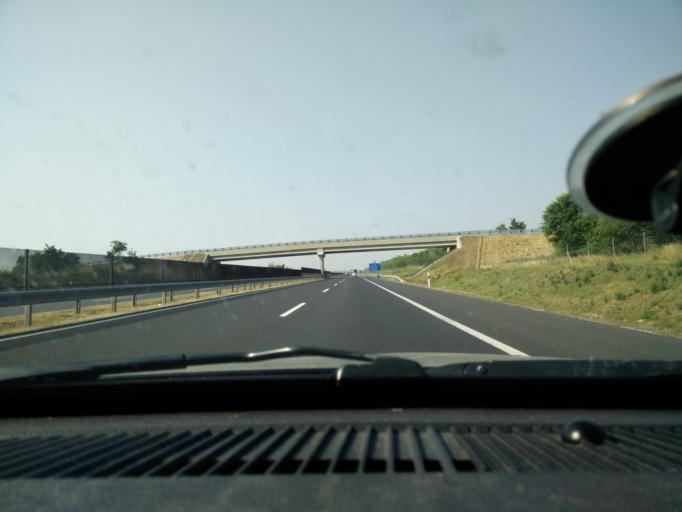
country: HU
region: Fejer
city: Ivancsa
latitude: 47.1888
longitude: 18.8123
